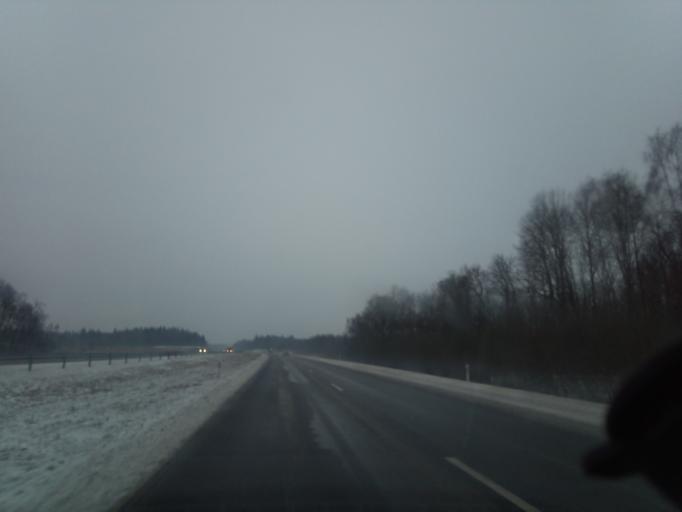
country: LT
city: Grigiskes
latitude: 54.8564
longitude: 25.0912
